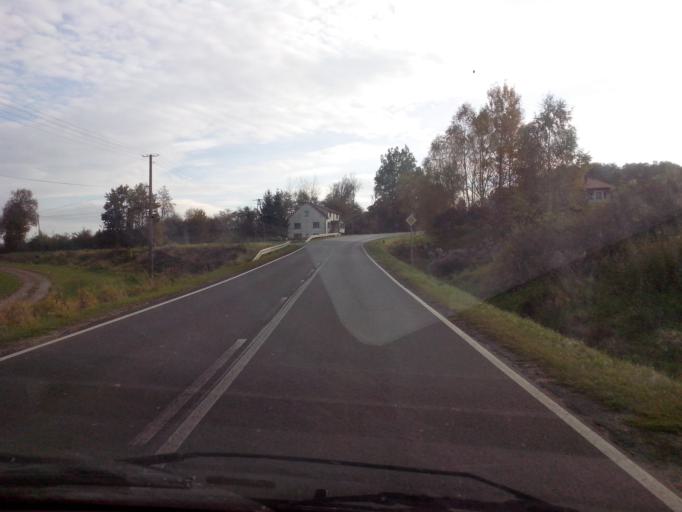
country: PL
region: Subcarpathian Voivodeship
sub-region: Powiat ropczycko-sedziszowski
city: Wielopole Skrzynskie
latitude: 49.9400
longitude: 21.6164
